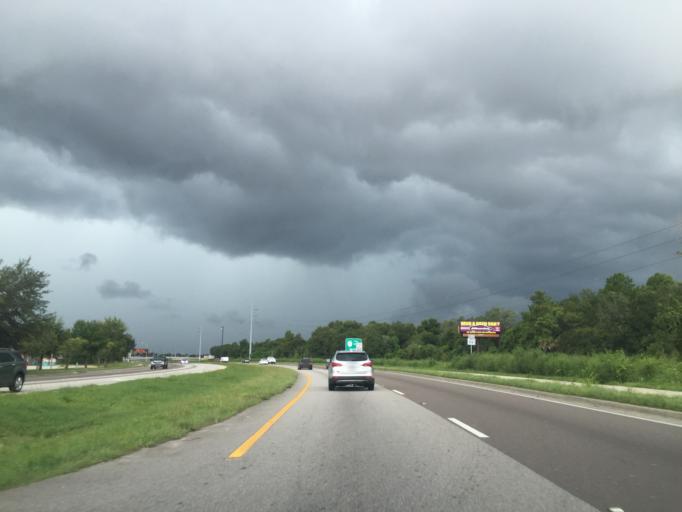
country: US
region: Florida
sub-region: Orange County
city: Lockhart
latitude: 28.6400
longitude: -81.4438
